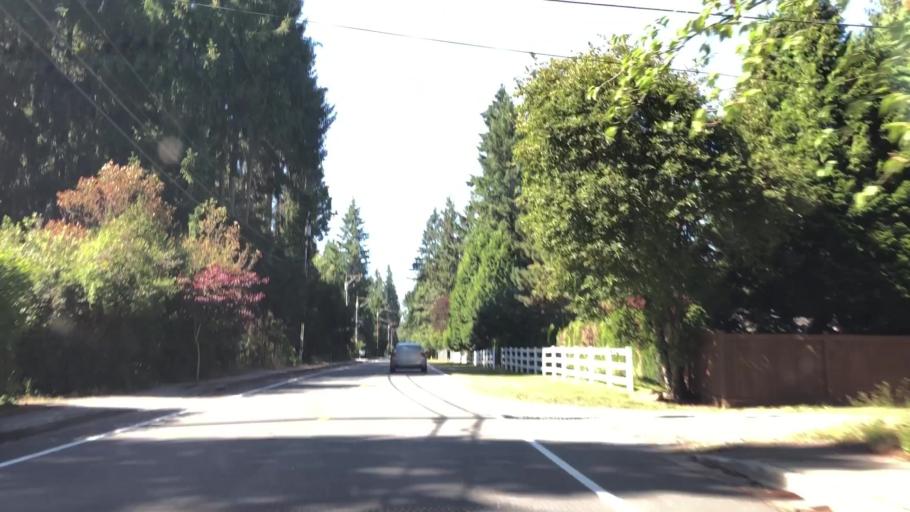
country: US
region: Washington
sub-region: King County
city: Woodinville
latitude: 47.7853
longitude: -122.1674
